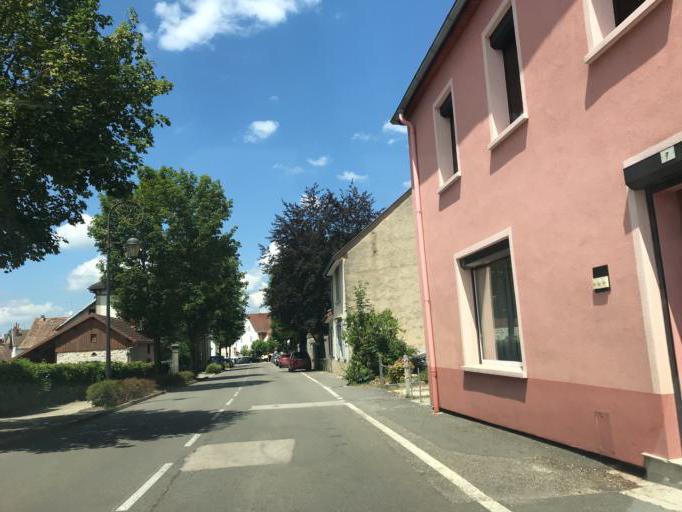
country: FR
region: Franche-Comte
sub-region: Departement du Jura
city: Clairvaux-les-Lacs
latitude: 46.5743
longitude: 5.7519
